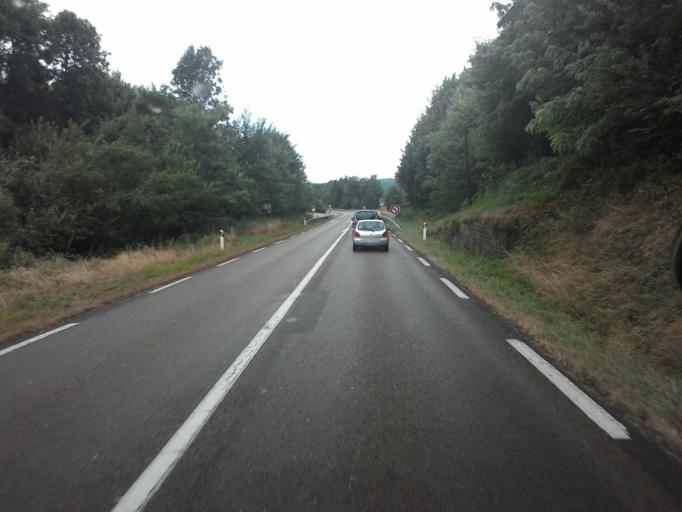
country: FR
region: Franche-Comte
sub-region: Departement du Jura
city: Poligny
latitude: 46.8492
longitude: 5.7071
